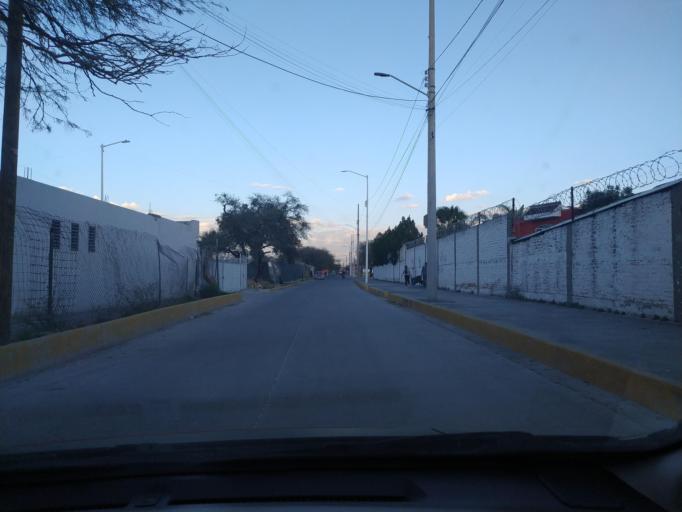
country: LA
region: Oudomxai
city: Muang La
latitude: 21.0136
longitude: 101.8718
